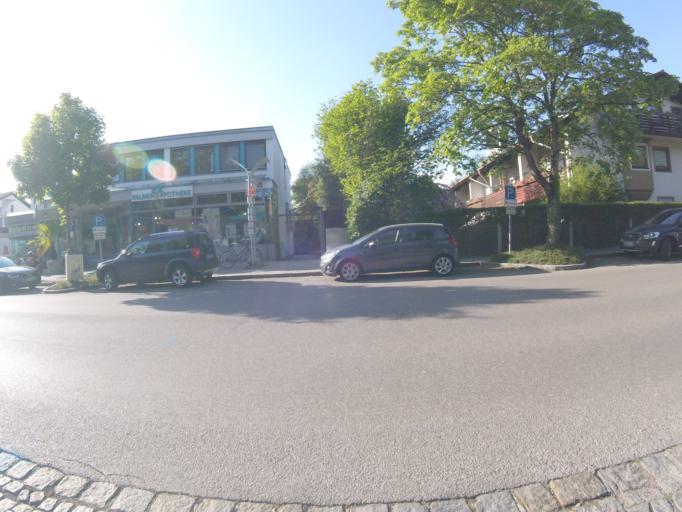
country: DE
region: Bavaria
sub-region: Upper Bavaria
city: Ottobrunn
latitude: 48.0617
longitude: 11.6741
